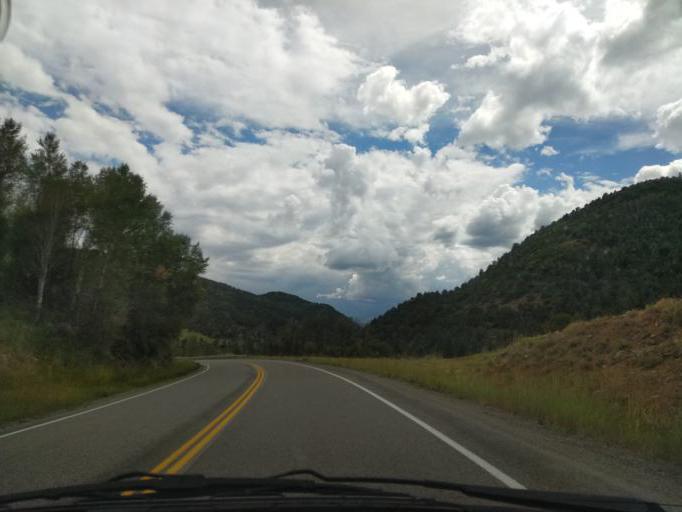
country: US
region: Colorado
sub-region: Delta County
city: Paonia
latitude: 39.0505
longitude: -107.3614
